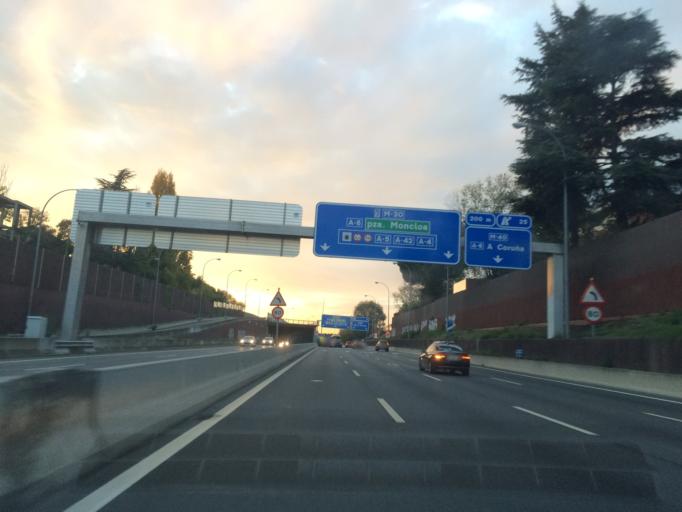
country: ES
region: Madrid
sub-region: Provincia de Madrid
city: Fuencarral-El Pardo
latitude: 40.4745
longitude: -3.7452
